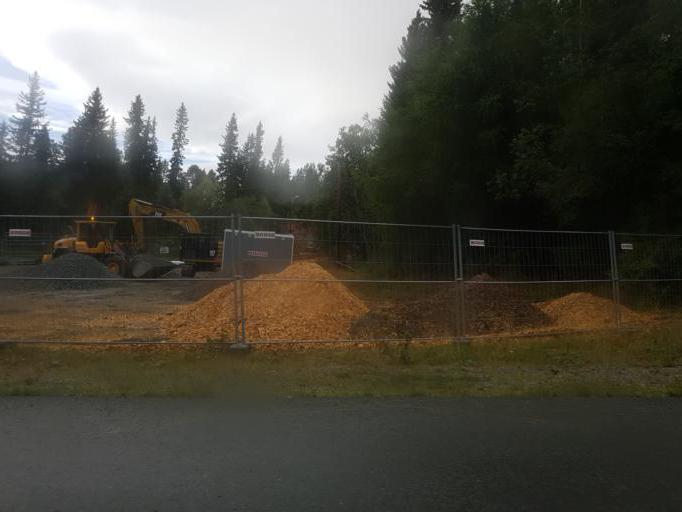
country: NO
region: Sor-Trondelag
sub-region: Trondheim
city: Trondheim
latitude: 63.4162
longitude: 10.2934
